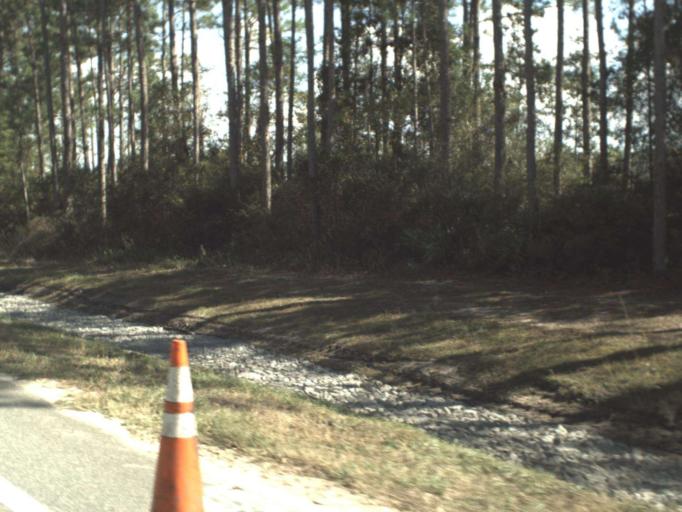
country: US
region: Florida
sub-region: Walton County
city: Freeport
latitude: 30.4737
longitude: -85.9833
